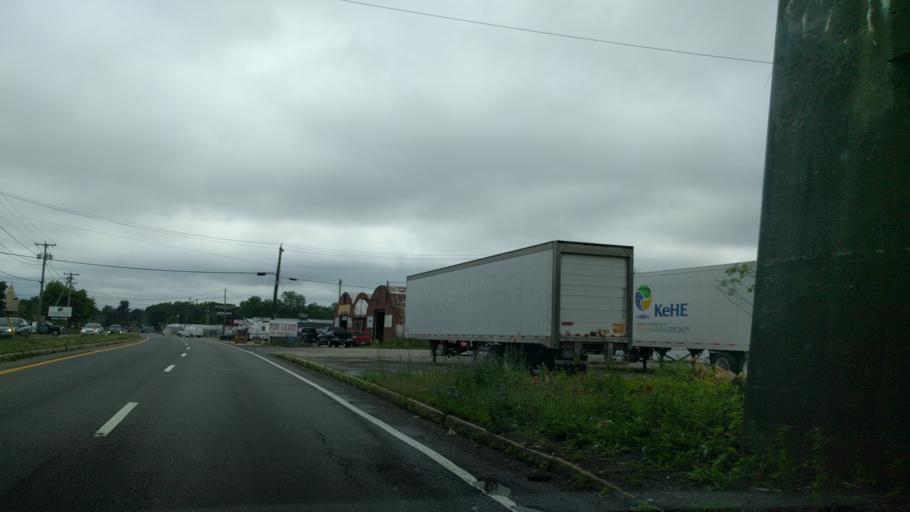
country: US
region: Massachusetts
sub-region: Worcester County
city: Sunderland
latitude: 42.2366
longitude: -71.7475
